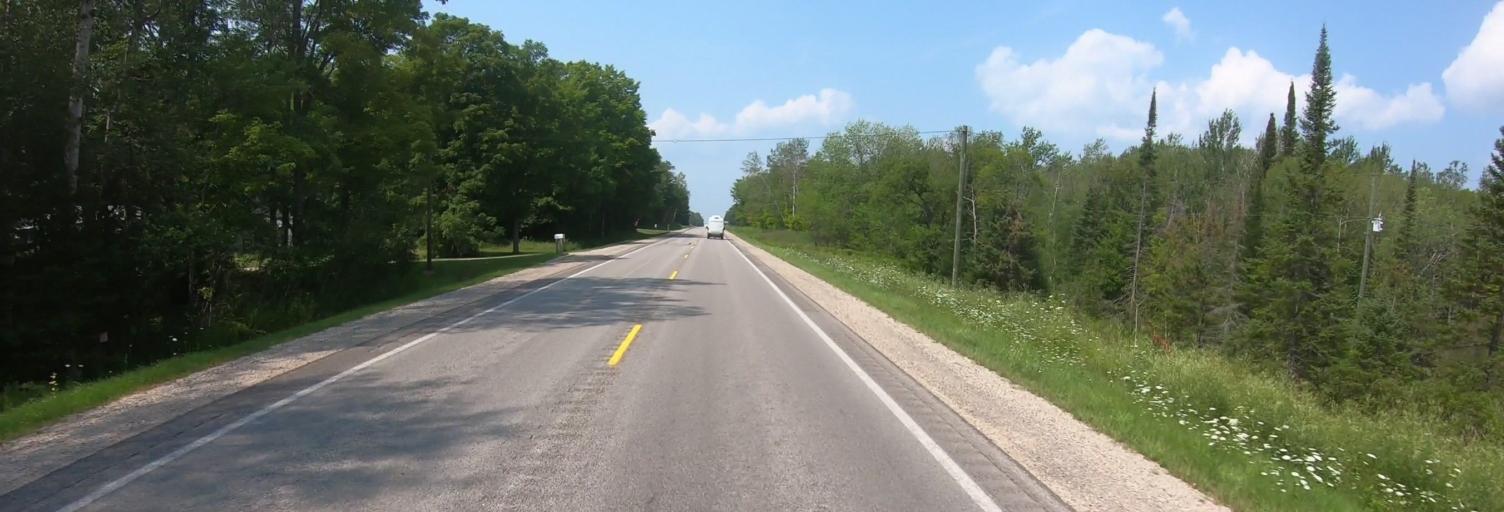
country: US
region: Michigan
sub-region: Luce County
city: Newberry
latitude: 46.3393
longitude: -85.7074
